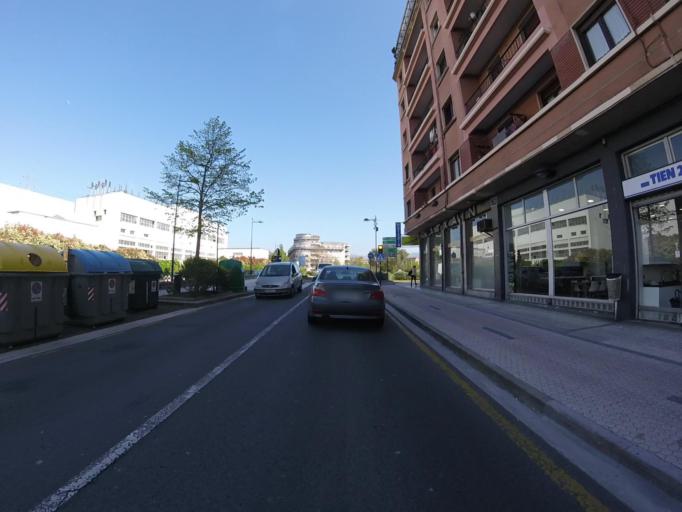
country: ES
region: Basque Country
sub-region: Provincia de Guipuzcoa
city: Errenteria
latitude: 43.3120
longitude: -1.8954
